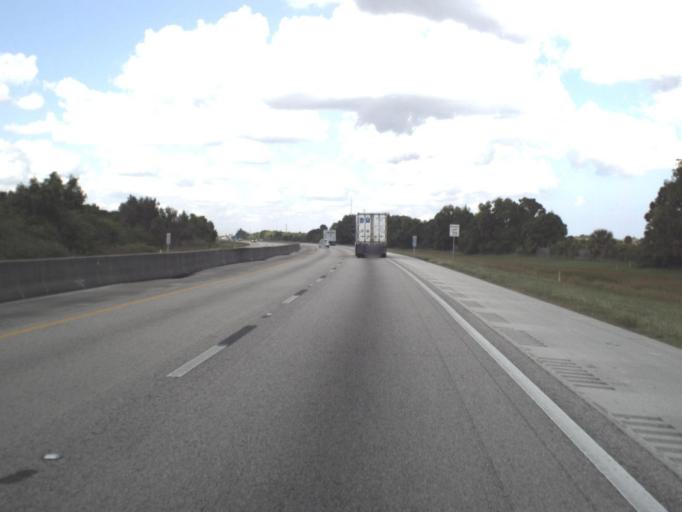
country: US
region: Florida
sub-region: Saint Lucie County
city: White City
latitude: 27.3553
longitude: -80.3748
